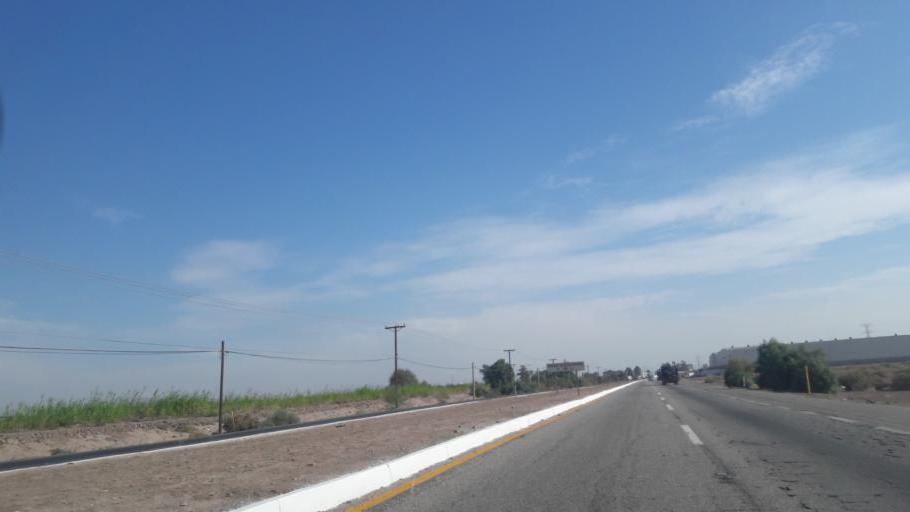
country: MX
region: Baja California
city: Progreso
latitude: 32.5849
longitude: -115.5955
